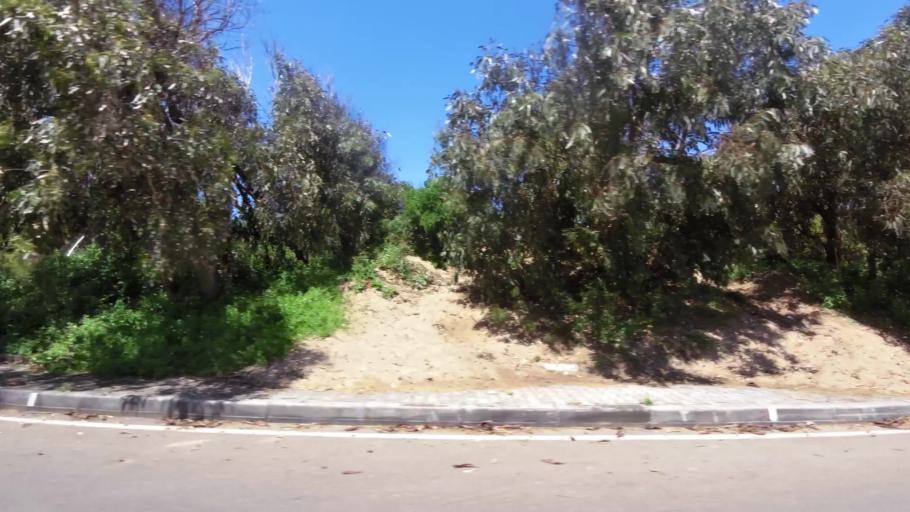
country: MA
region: Grand Casablanca
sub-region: Nouaceur
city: Dar Bouazza
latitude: 33.5362
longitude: -7.7847
